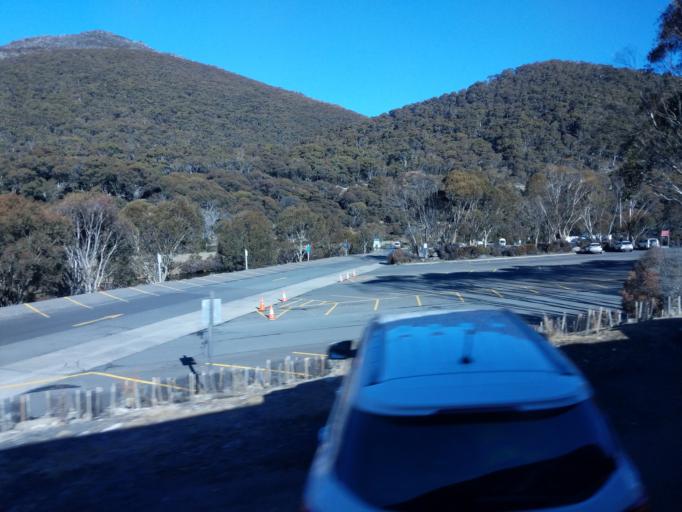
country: AU
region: New South Wales
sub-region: Snowy River
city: Jindabyne
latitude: -36.4975
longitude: 148.3144
